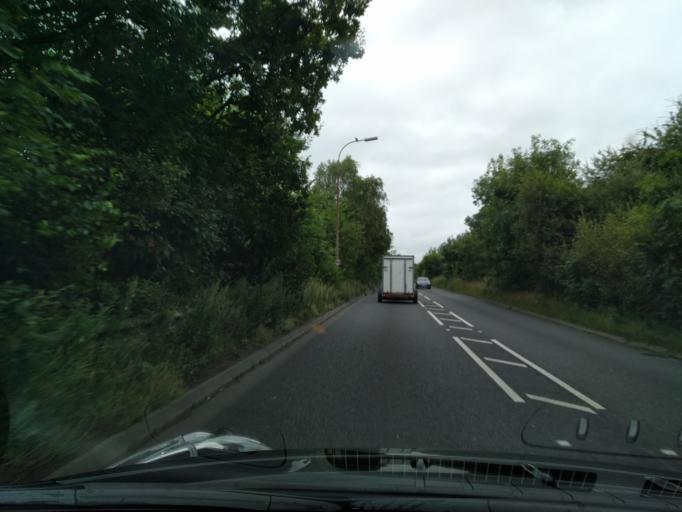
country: GB
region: England
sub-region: Warrington
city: Culcheth
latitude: 53.4319
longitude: -2.5068
